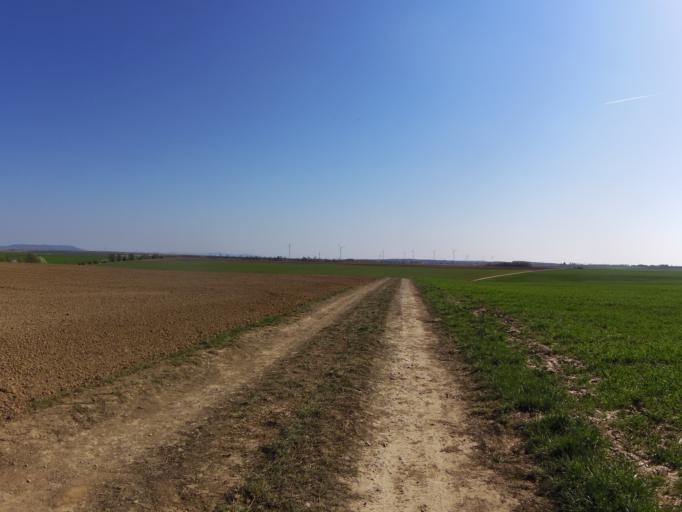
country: DE
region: Bavaria
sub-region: Regierungsbezirk Unterfranken
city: Biebelried
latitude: 49.8183
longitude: 10.1015
